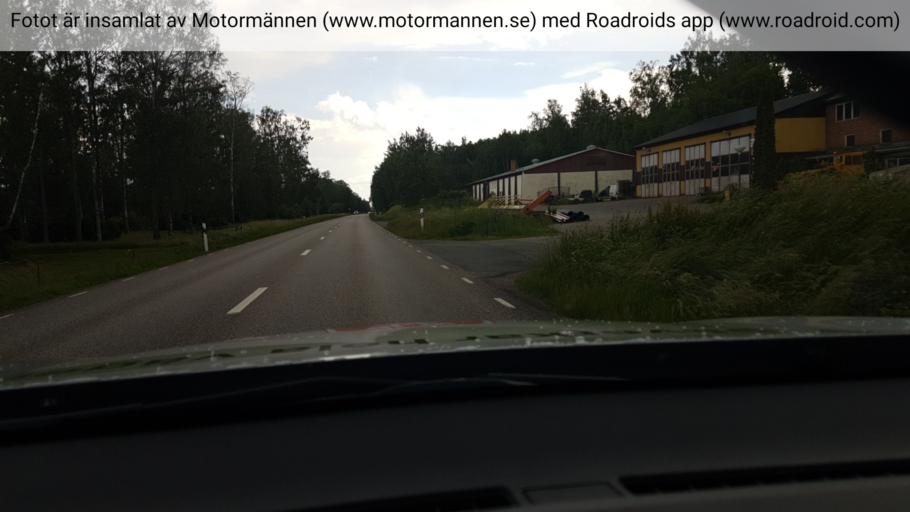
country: SE
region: Vaestra Goetaland
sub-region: Hjo Kommun
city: Hjo
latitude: 58.1643
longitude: 14.2091
